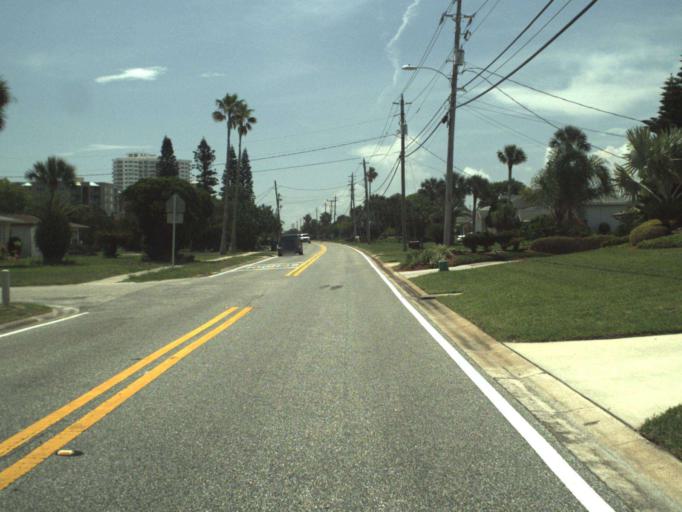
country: US
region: Florida
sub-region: Volusia County
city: Daytona Beach Shores
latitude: 29.1744
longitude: -80.9858
